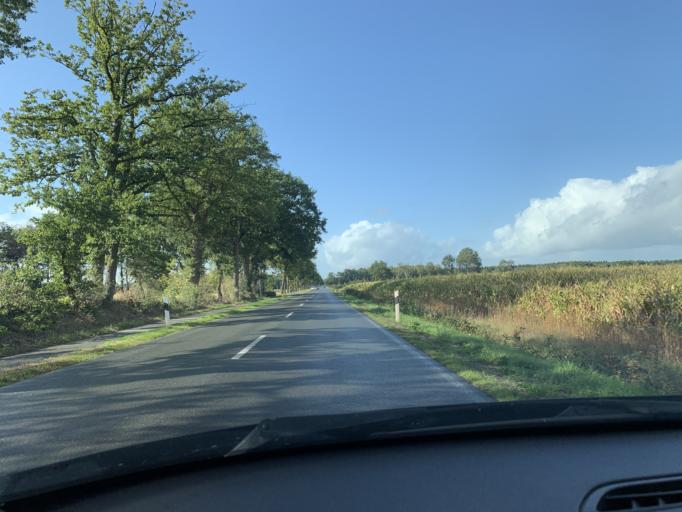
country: DE
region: Lower Saxony
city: Bad Zwischenahn
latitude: 53.1841
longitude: 7.9283
